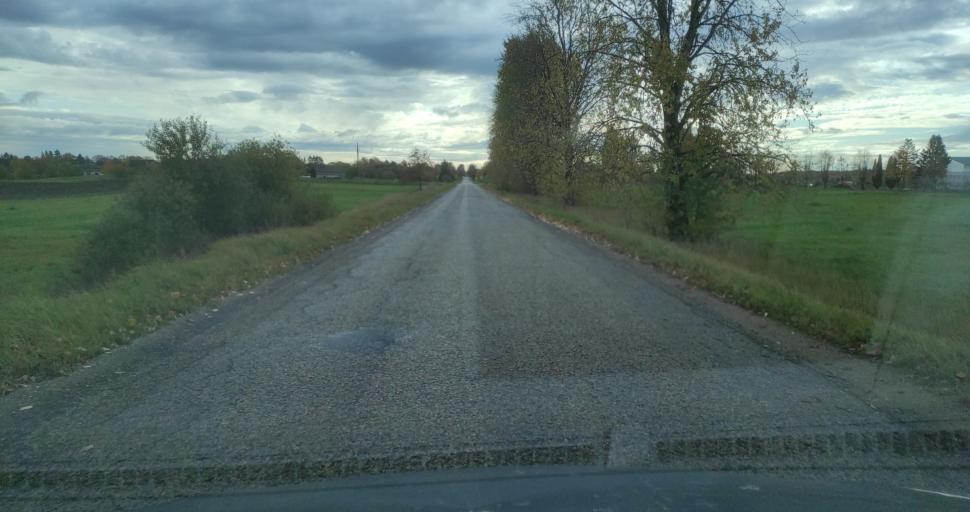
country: LV
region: Vainode
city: Vainode
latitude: 56.5747
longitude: 21.8907
